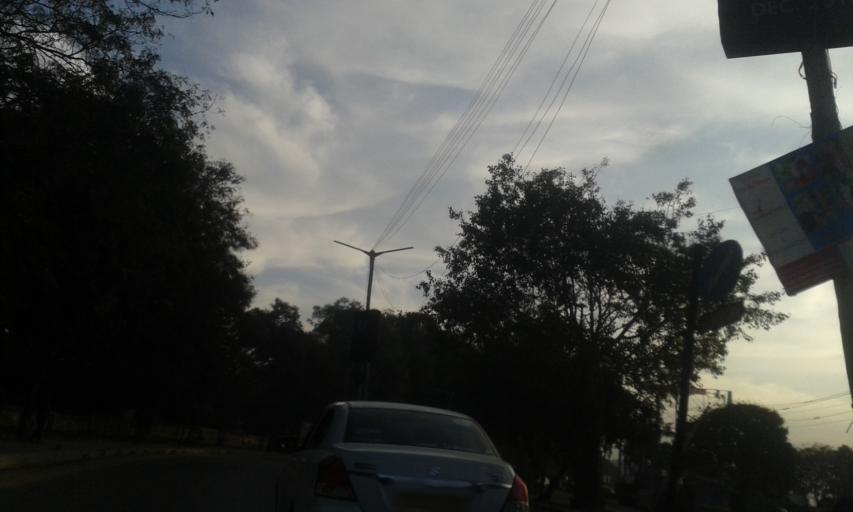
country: IN
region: Karnataka
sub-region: Bangalore Rural
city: Hoskote
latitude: 12.9936
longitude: 77.7575
